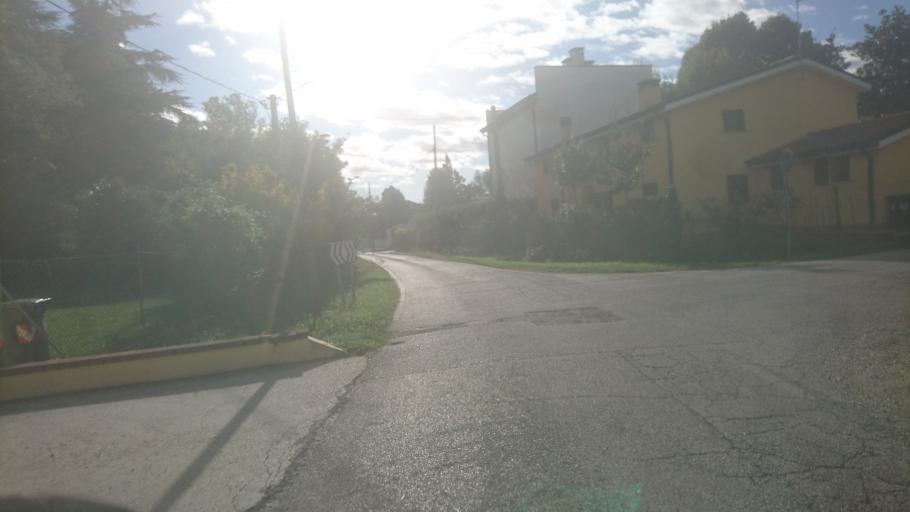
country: IT
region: Veneto
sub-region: Provincia di Padova
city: Abano Terme
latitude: 45.3446
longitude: 11.8057
